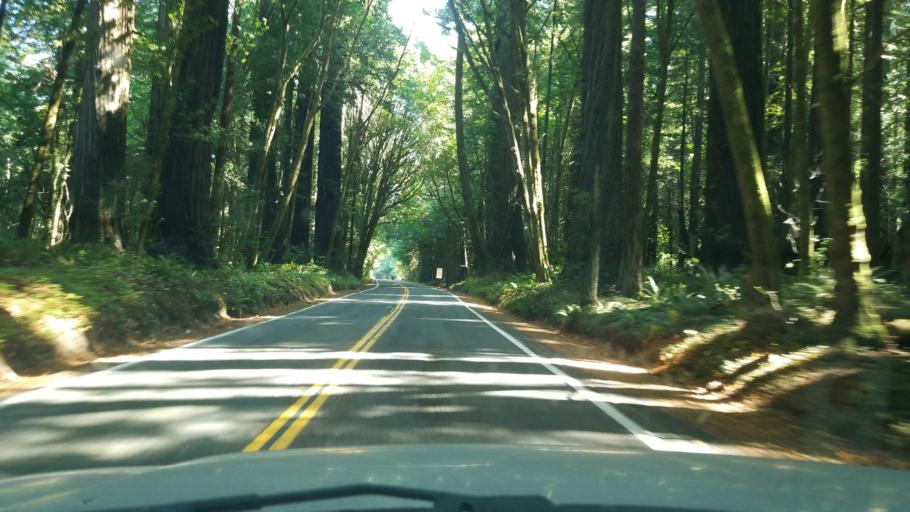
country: US
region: California
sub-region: Humboldt County
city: Rio Dell
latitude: 40.4415
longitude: -124.0301
